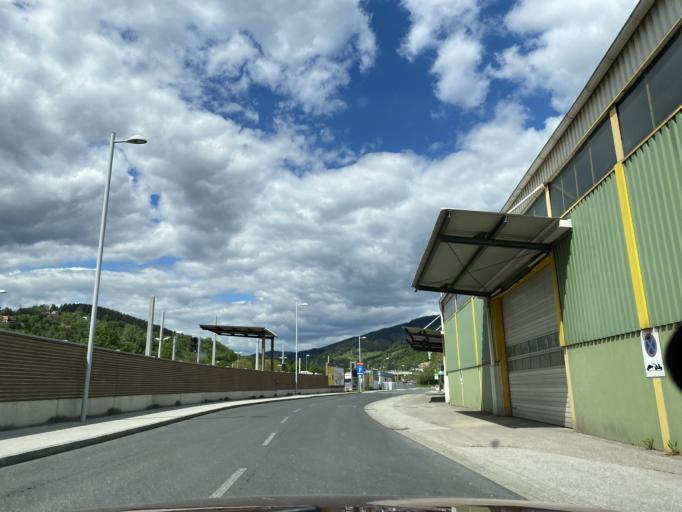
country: AT
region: Carinthia
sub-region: Politischer Bezirk Wolfsberg
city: Wolfsberg
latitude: 46.8430
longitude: 14.8393
